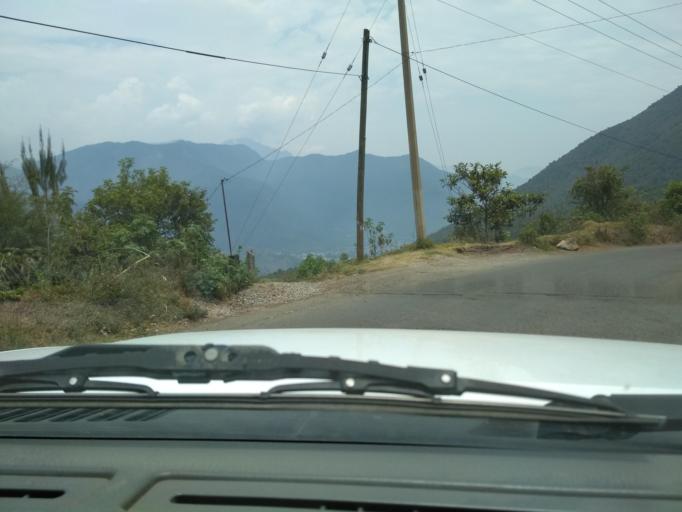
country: MX
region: Veracruz
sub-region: Camerino Z. Mendoza
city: La Cuesta
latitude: 18.7873
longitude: -97.1661
